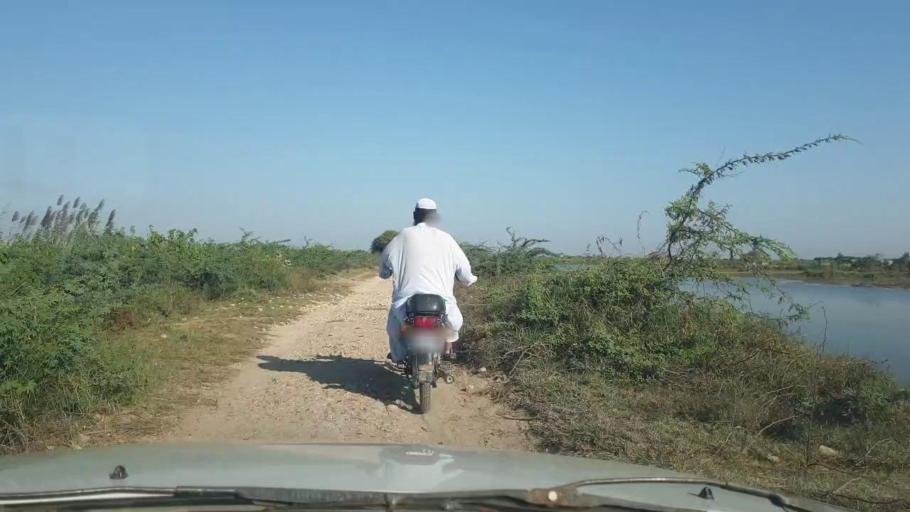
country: PK
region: Sindh
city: Chuhar Jamali
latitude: 24.5465
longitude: 67.9110
